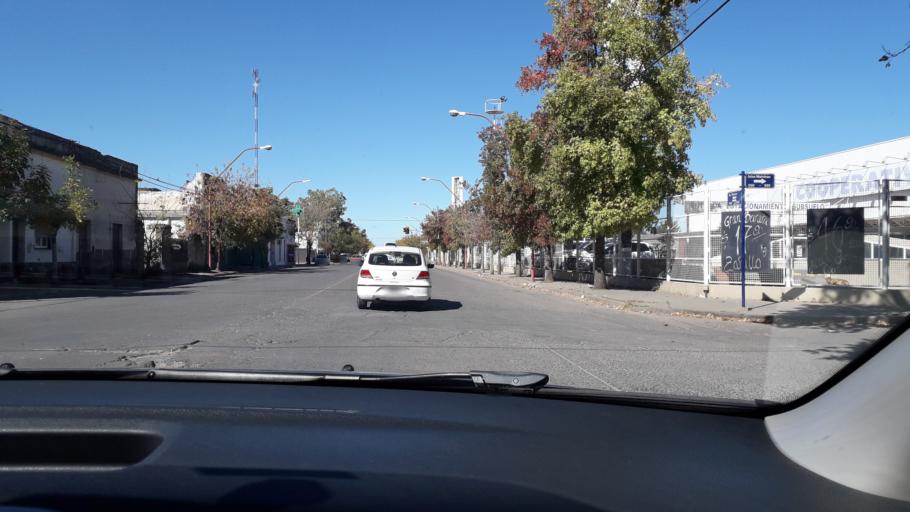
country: AR
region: Buenos Aires
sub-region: Partido de Azul
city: Azul
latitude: -36.7849
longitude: -59.8498
